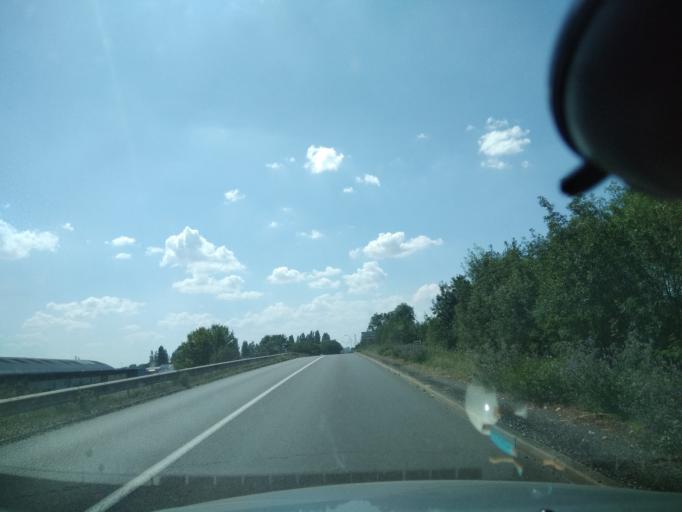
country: FR
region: Centre
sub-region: Departement d'Indre-et-Loire
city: Saint-Pierre-des-Corps
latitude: 47.3811
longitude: 0.7408
